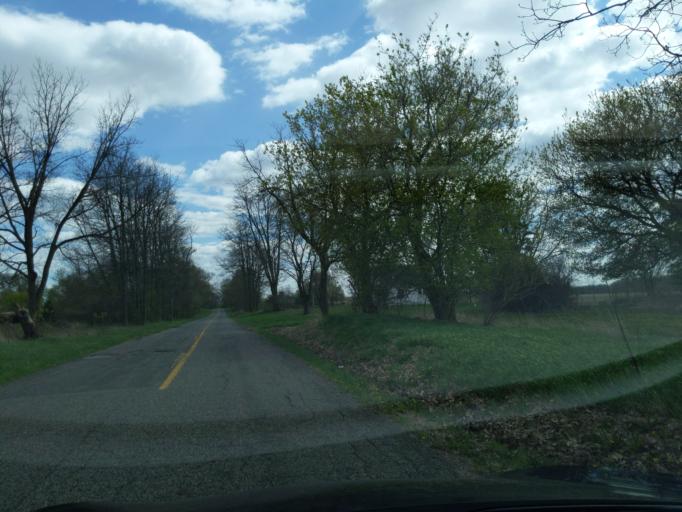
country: US
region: Michigan
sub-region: Ingham County
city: Leslie
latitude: 42.4786
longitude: -84.5412
